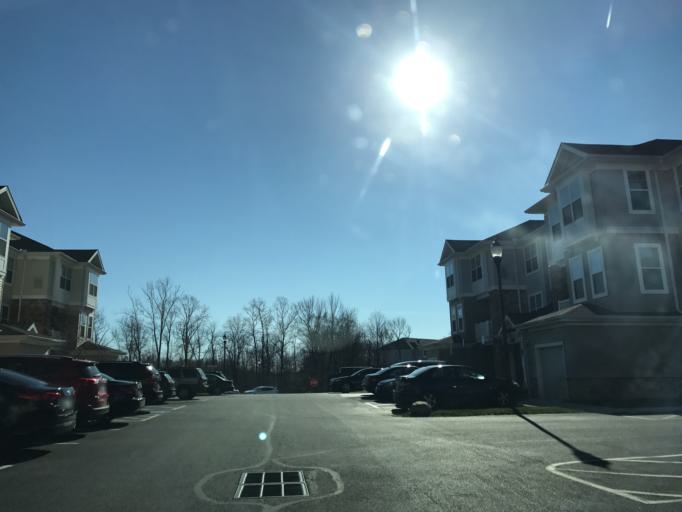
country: US
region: Maryland
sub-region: Harford County
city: Riverside
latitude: 39.4872
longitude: -76.2393
